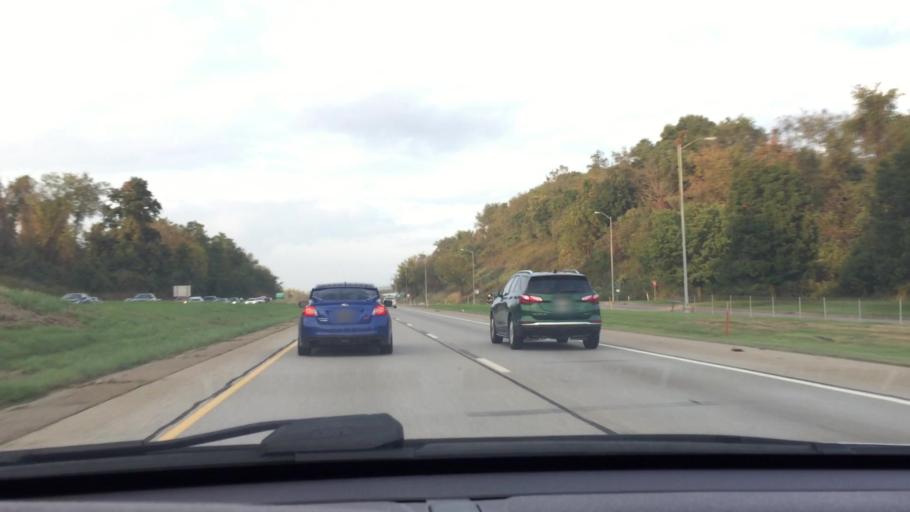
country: US
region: Pennsylvania
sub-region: Allegheny County
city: Bridgeville
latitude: 40.3325
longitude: -80.1374
